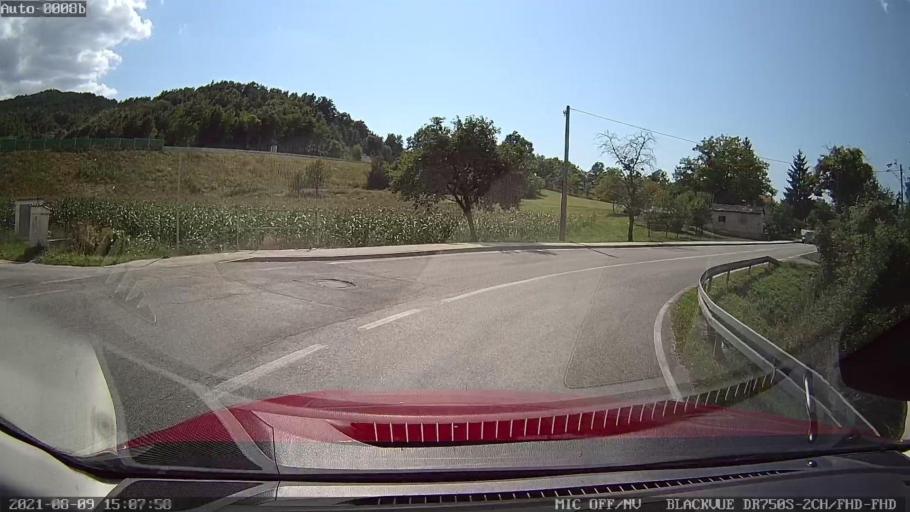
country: HR
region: Istarska
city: Pazin
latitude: 45.2443
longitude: 13.9586
